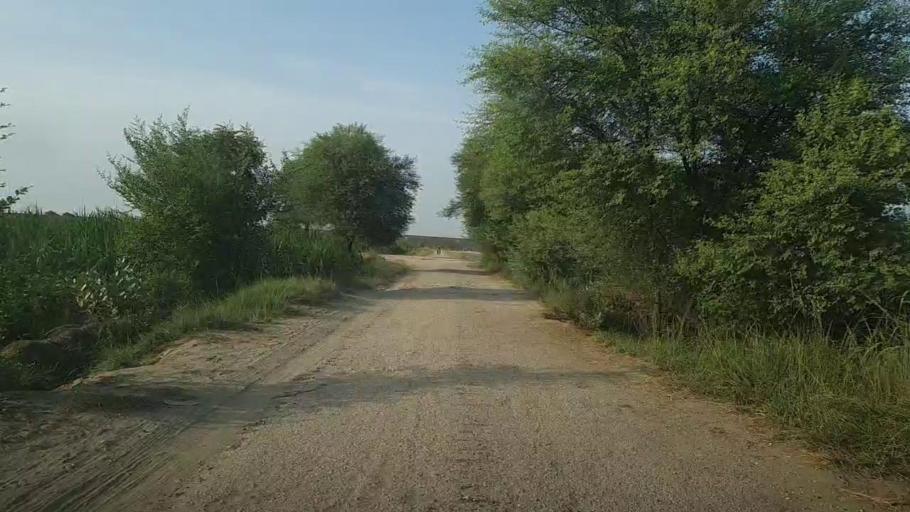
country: PK
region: Sindh
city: Ubauro
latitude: 28.3307
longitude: 69.7981
